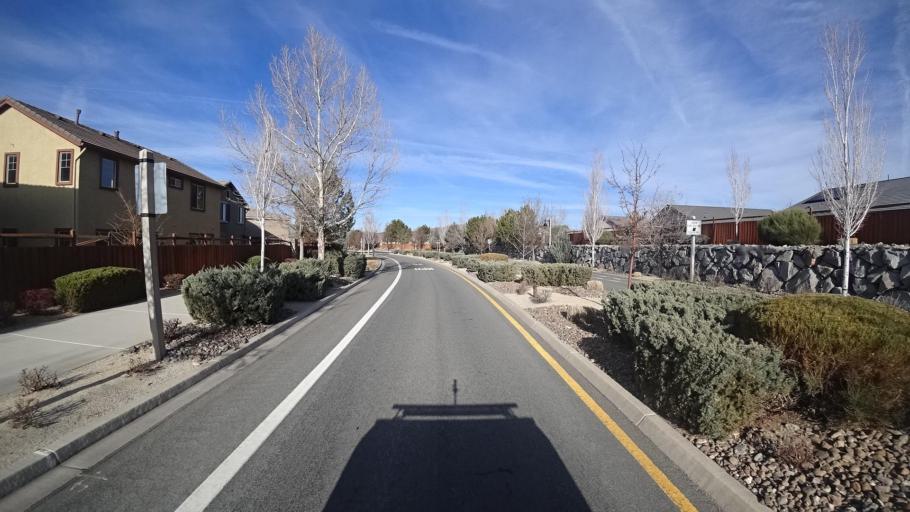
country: US
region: Nevada
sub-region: Washoe County
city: Spanish Springs
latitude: 39.6233
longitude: -119.6719
